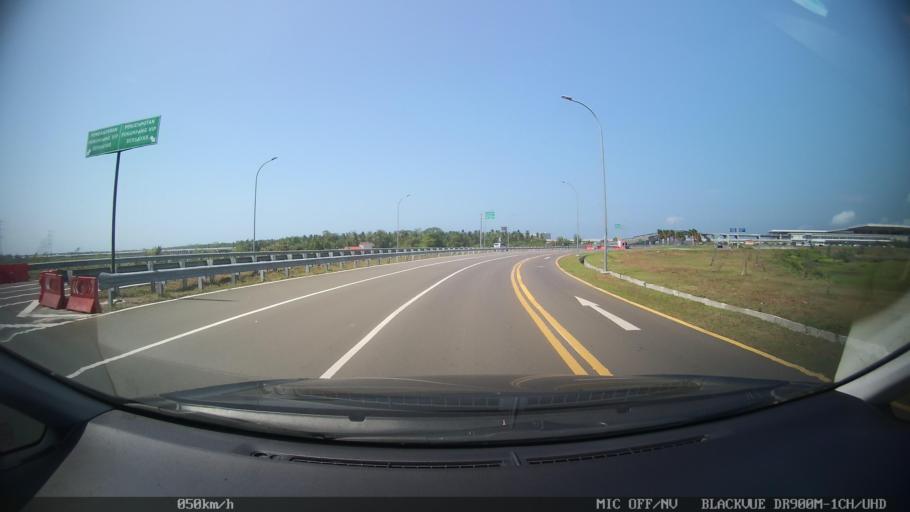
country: ID
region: Daerah Istimewa Yogyakarta
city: Srandakan
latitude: -7.8941
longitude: 110.0641
